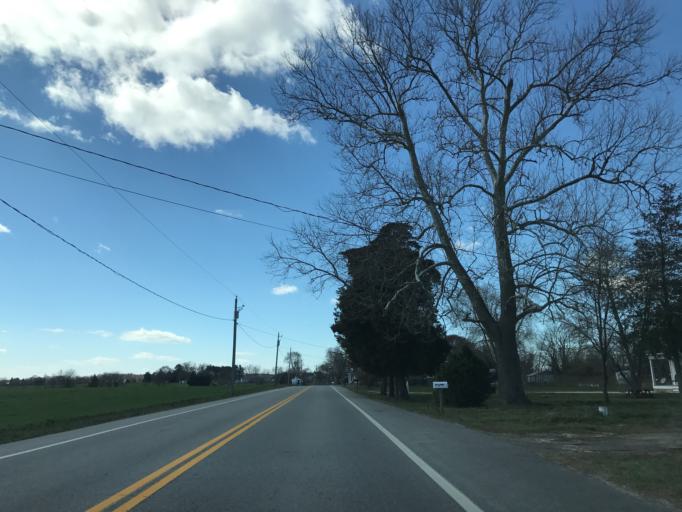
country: US
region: Maryland
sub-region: Caroline County
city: Greensboro
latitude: 39.0925
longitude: -75.8720
